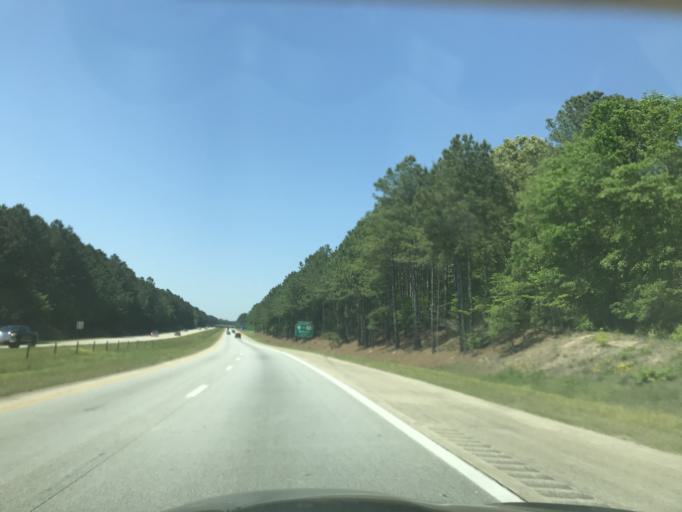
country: US
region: North Carolina
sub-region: Johnston County
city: Benson
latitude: 35.4121
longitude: -78.5246
